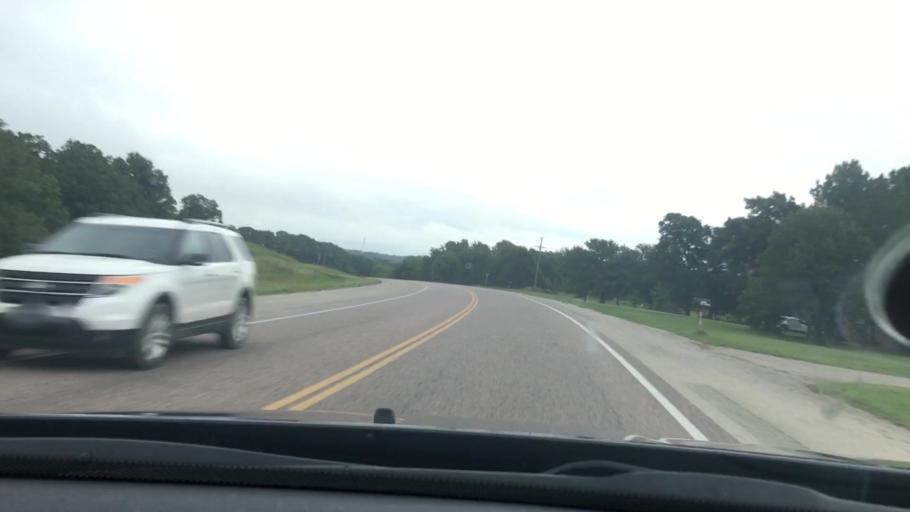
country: US
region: Oklahoma
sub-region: Pontotoc County
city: Ada
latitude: 34.7832
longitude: -96.5754
